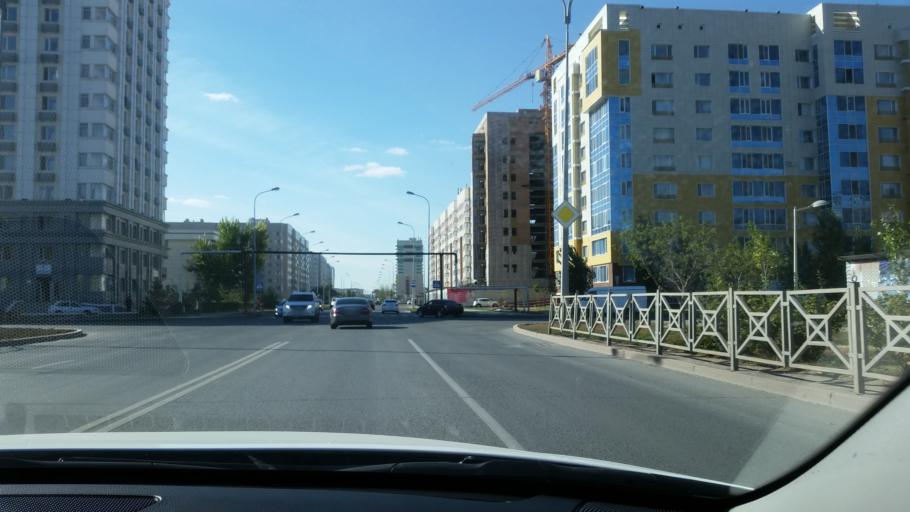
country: KZ
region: Astana Qalasy
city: Astana
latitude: 51.1166
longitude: 71.4247
